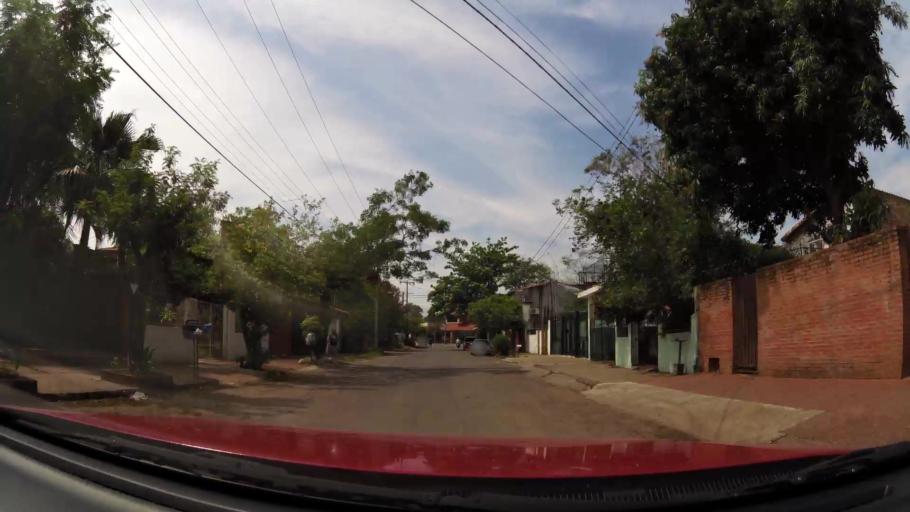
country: PY
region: Asuncion
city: Asuncion
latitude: -25.2702
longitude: -57.5874
